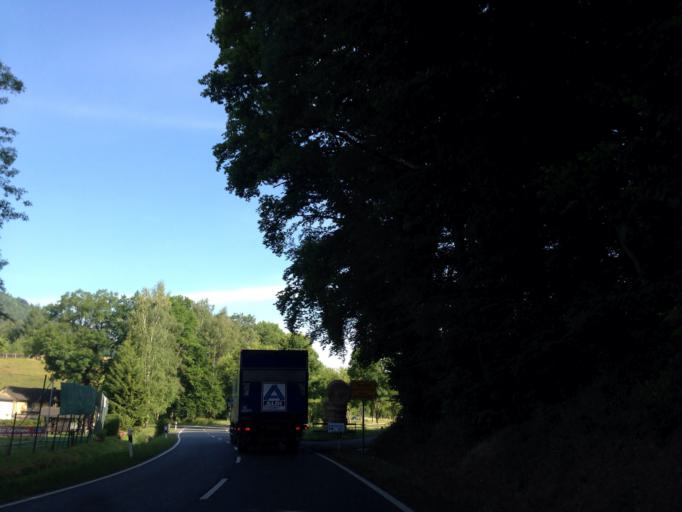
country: DE
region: Thuringia
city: Rudolstadt
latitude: 50.7809
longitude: 11.3136
